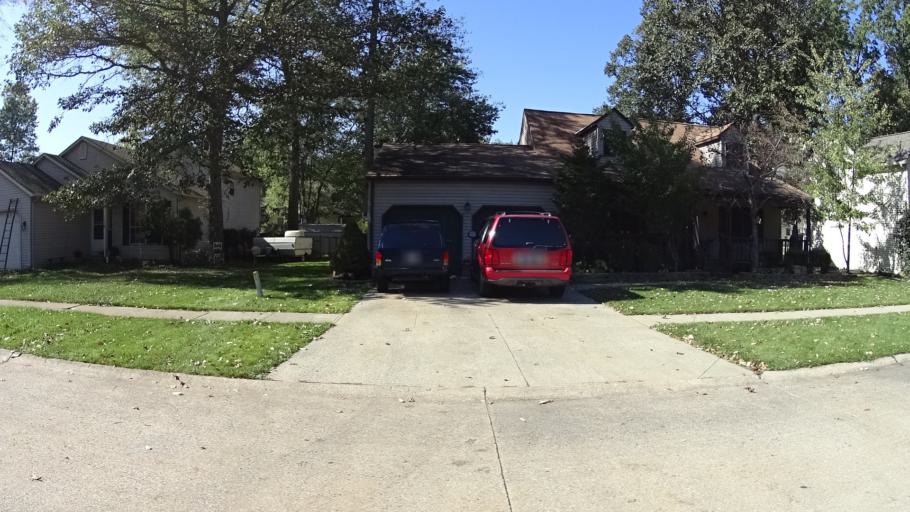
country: US
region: Ohio
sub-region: Lorain County
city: Vermilion-on-the-Lake
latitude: 41.4220
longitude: -82.3185
